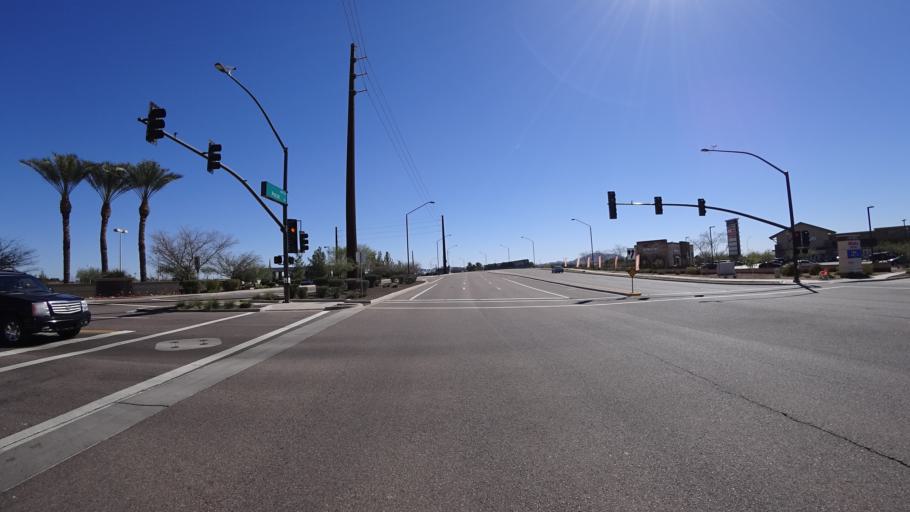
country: US
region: Arizona
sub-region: Maricopa County
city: Gilbert
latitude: 33.2950
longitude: -111.7473
